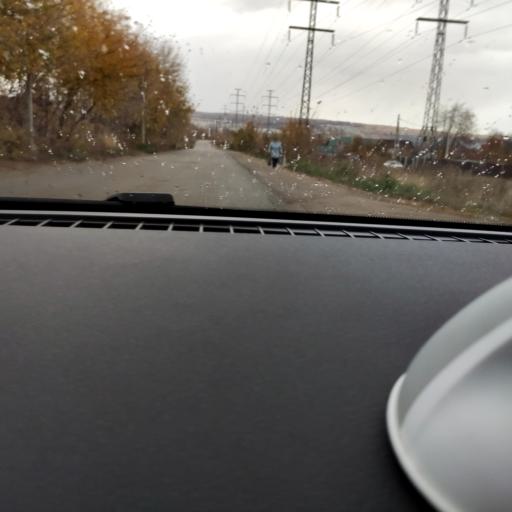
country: RU
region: Samara
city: Petra-Dubrava
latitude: 53.2946
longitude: 50.2953
